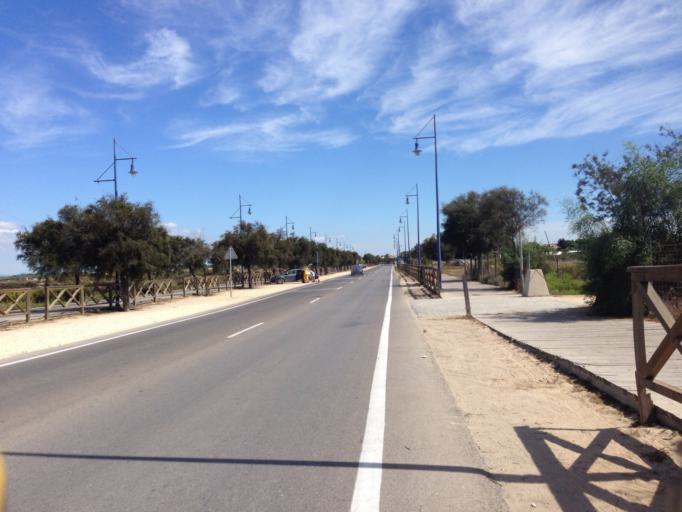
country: ES
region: Andalusia
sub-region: Provincia de Cadiz
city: Chiclana de la Frontera
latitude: 36.3866
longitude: -6.2063
